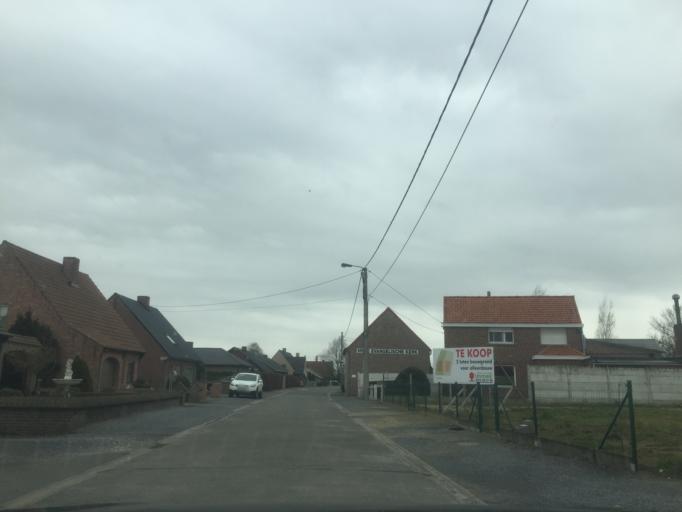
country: BE
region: Flanders
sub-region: Provincie West-Vlaanderen
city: Oostrozebeke
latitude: 50.9168
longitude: 3.3109
